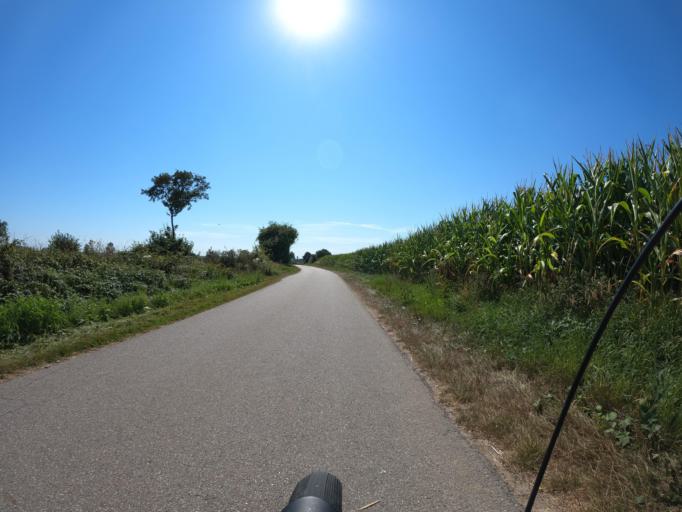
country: DE
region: Schleswig-Holstein
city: Steinberg
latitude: 54.7658
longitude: 9.7772
